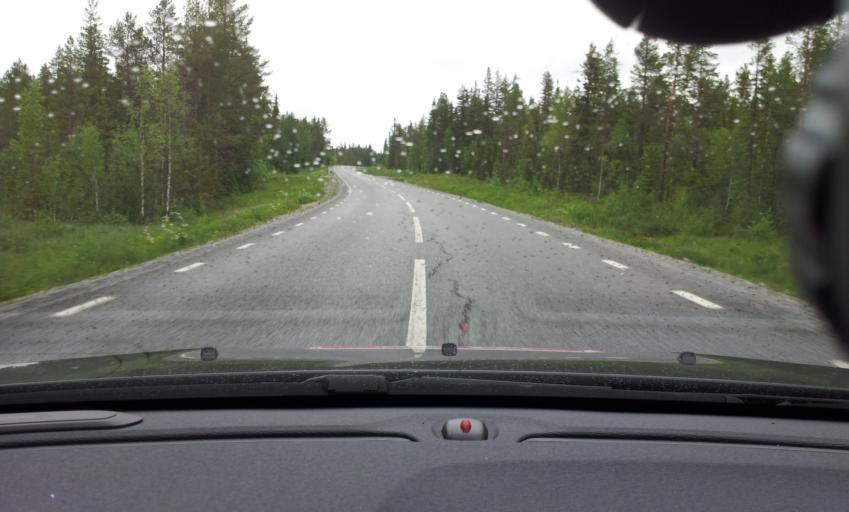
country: SE
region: Jaemtland
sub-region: OEstersunds Kommun
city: Lit
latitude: 63.6969
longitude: 14.6851
